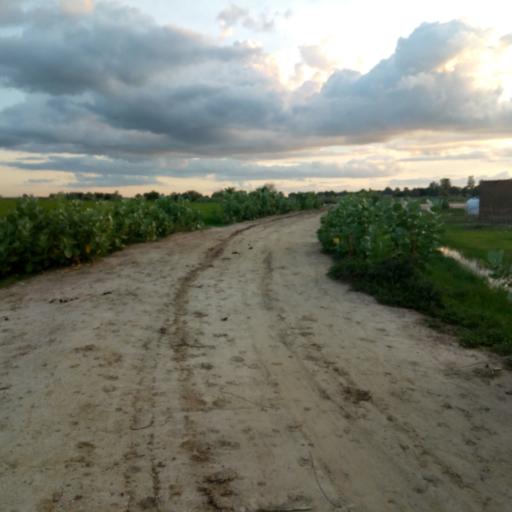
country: ML
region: Segou
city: Niono
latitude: 14.3089
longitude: -5.9547
